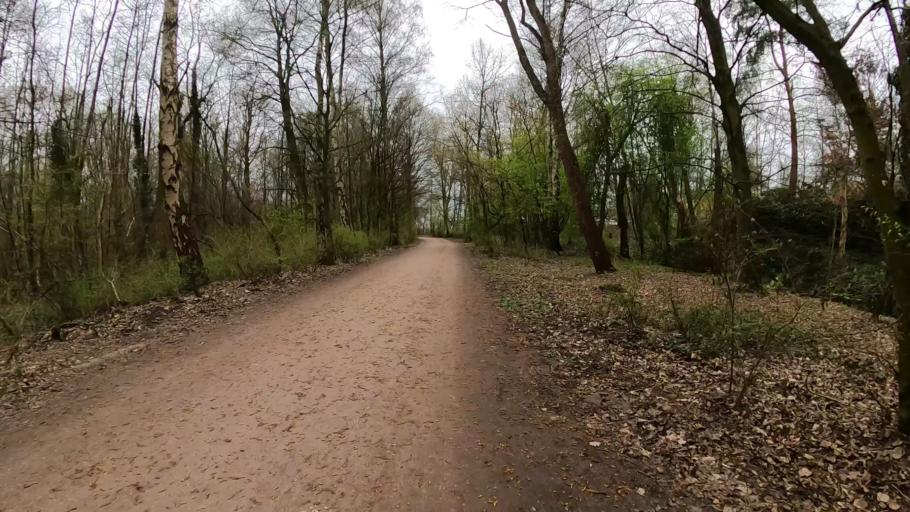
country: DE
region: Hamburg
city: Langenhorn
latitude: 53.6701
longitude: 9.9903
